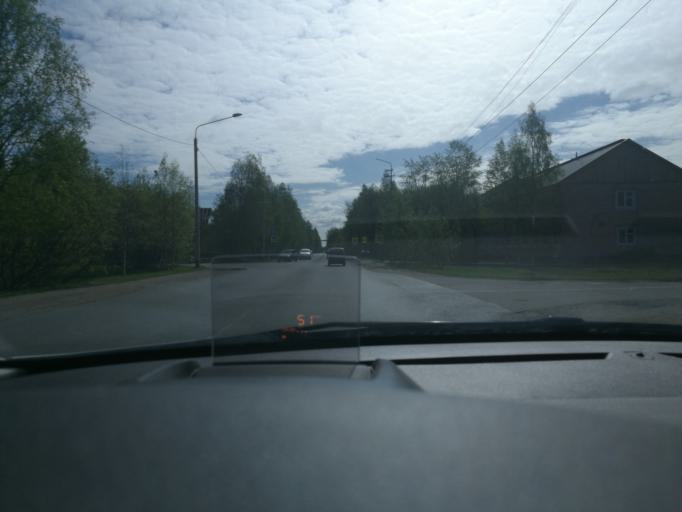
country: RU
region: Arkhangelskaya
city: Arkhangel'sk
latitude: 64.5937
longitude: 40.5828
